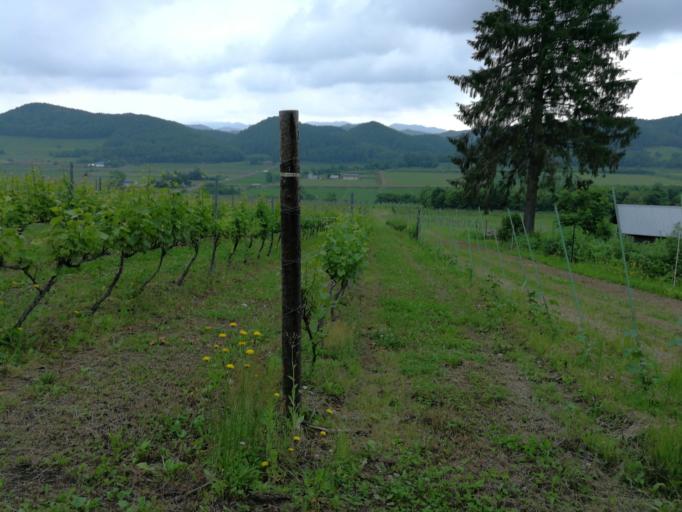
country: JP
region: Hokkaido
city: Iwamizawa
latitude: 43.1909
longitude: 141.8174
